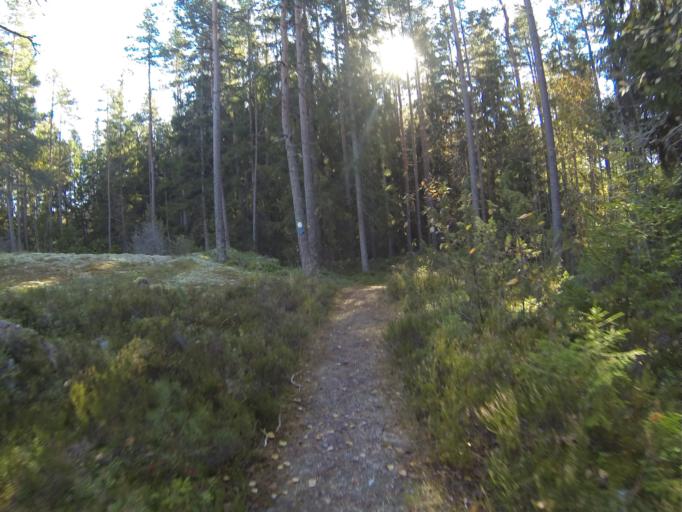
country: FI
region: Varsinais-Suomi
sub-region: Salo
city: Saerkisalo
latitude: 60.2048
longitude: 22.9392
